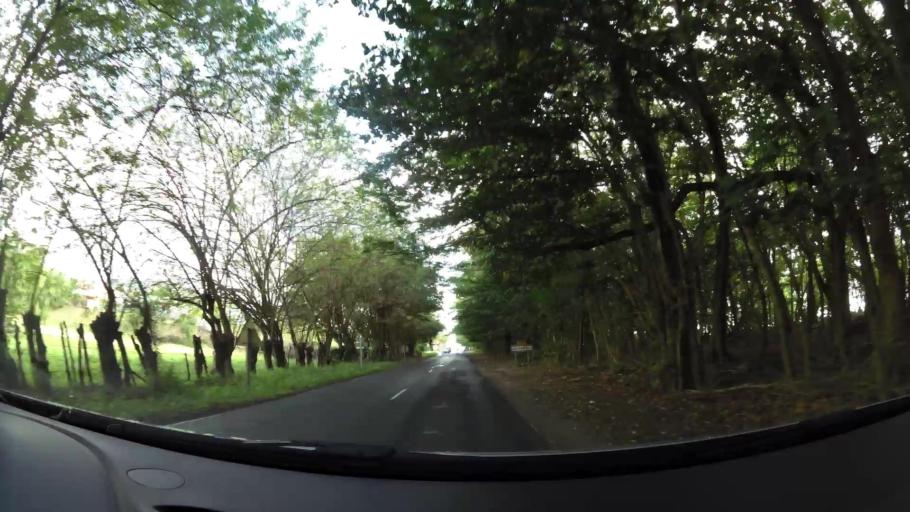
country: MQ
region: Martinique
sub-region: Martinique
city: Les Trois-Ilets
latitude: 14.4777
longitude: -61.0335
